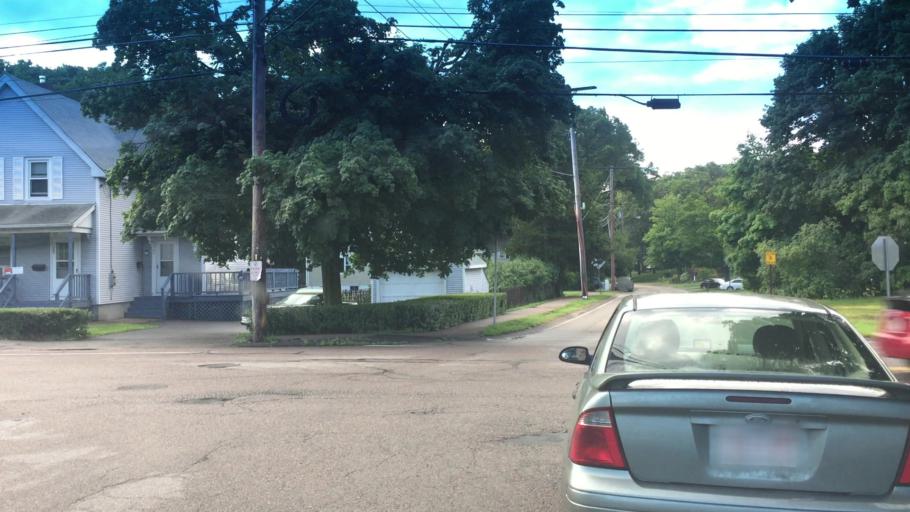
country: US
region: Massachusetts
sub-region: Norfolk County
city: Walpole
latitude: 42.1550
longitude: -71.2221
